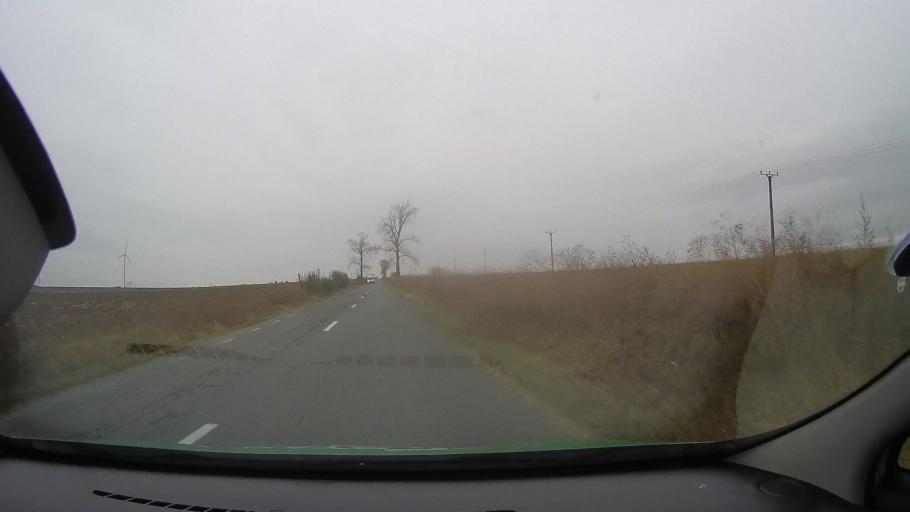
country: RO
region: Constanta
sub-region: Comuna Pantelimon
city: Pantelimon
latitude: 44.5649
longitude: 28.3189
